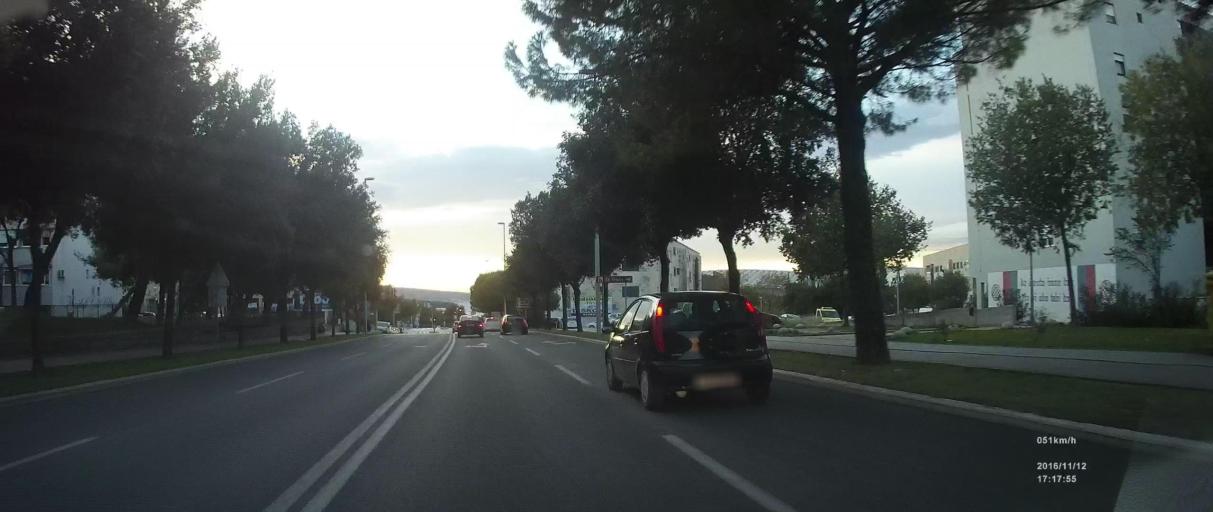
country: HR
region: Splitsko-Dalmatinska
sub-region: Grad Split
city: Split
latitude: 43.5186
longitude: 16.4371
